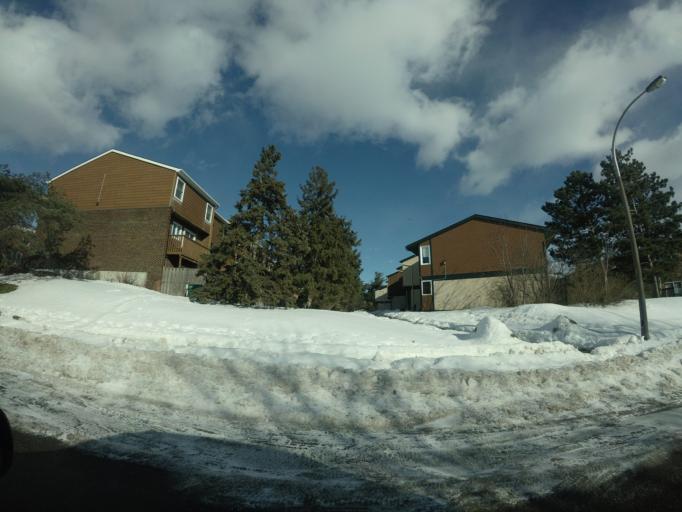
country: CA
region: Ontario
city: Ottawa
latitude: 45.4243
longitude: -75.6052
